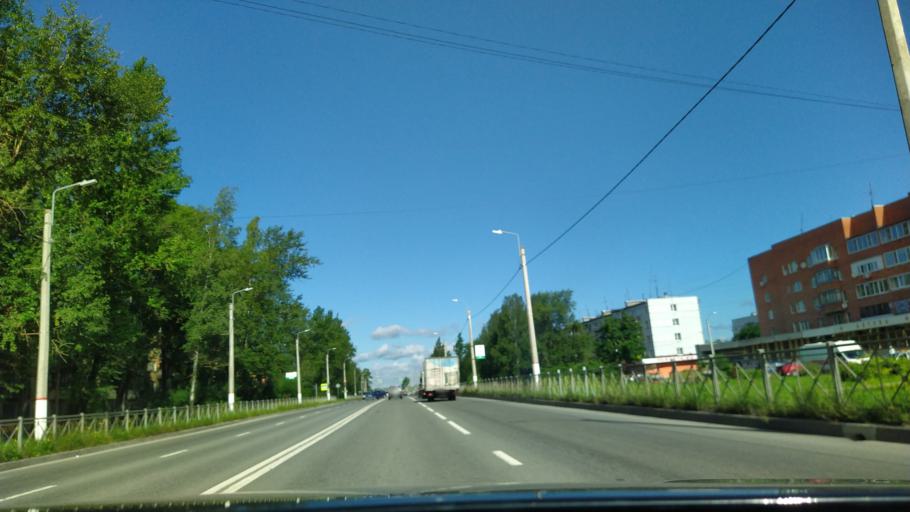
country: RU
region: Leningrad
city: Tosno
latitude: 59.5571
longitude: 30.8477
